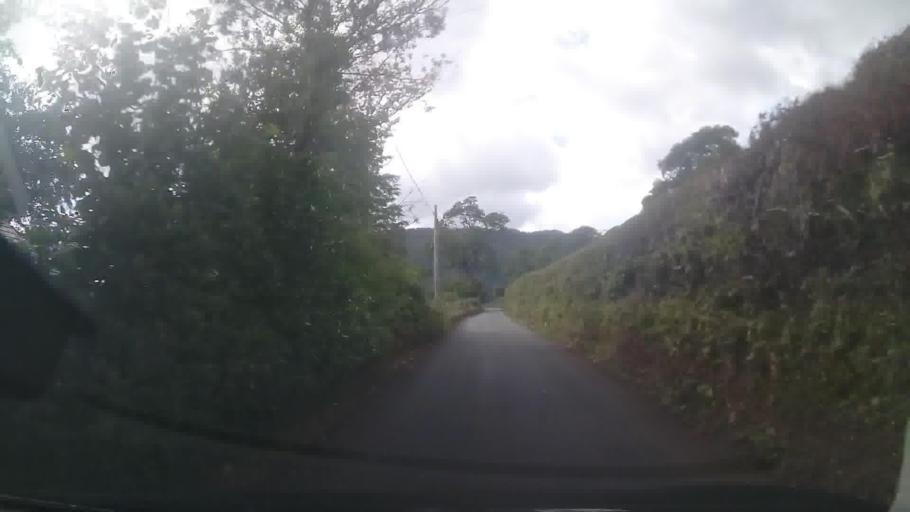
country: GB
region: Wales
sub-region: Gwynedd
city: Corris
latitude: 52.7265
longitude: -3.6811
